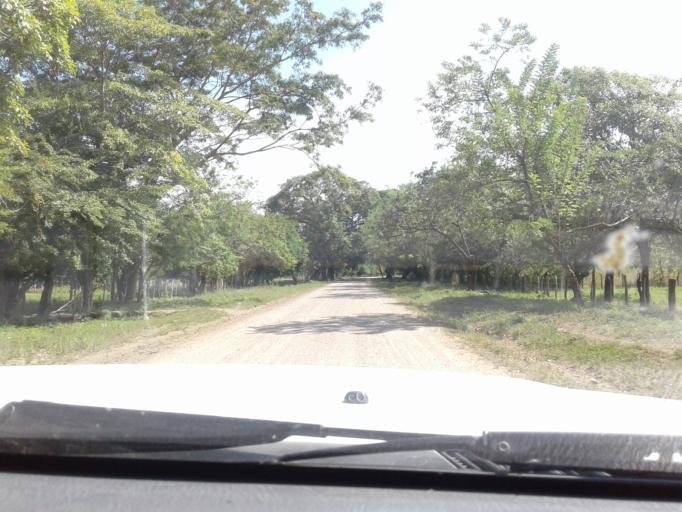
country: NI
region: Rivas
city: Belen
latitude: 11.6392
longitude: -85.9133
